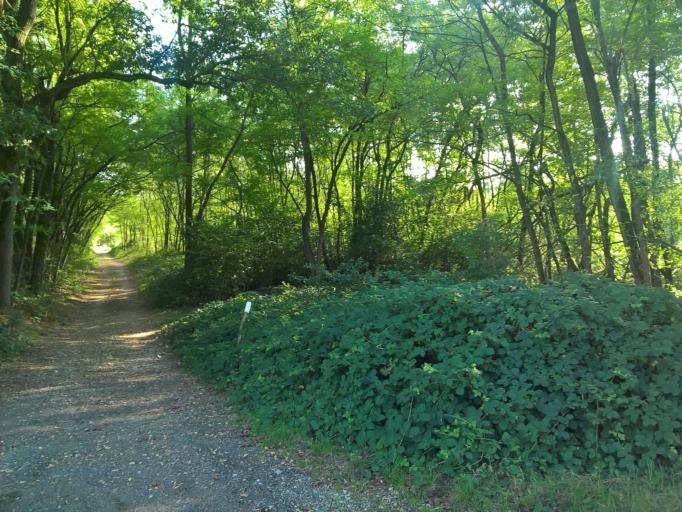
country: IT
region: Piedmont
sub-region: Provincia di Novara
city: Cressa
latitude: 45.6662
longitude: 8.4970
